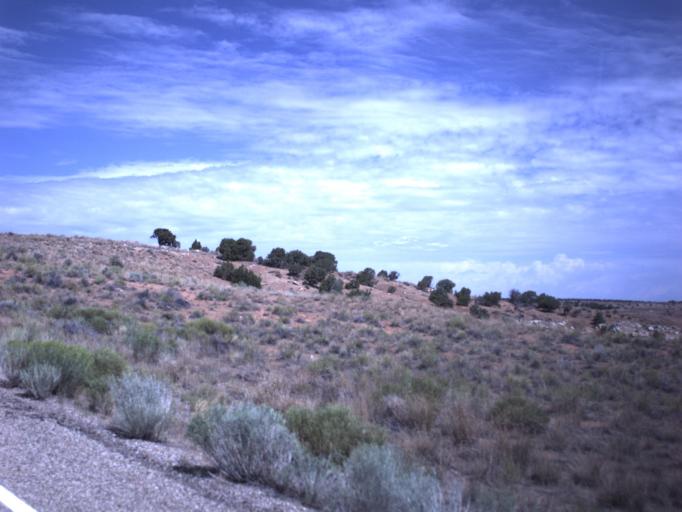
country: US
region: Utah
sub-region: Uintah County
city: Naples
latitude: 40.1413
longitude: -109.2747
